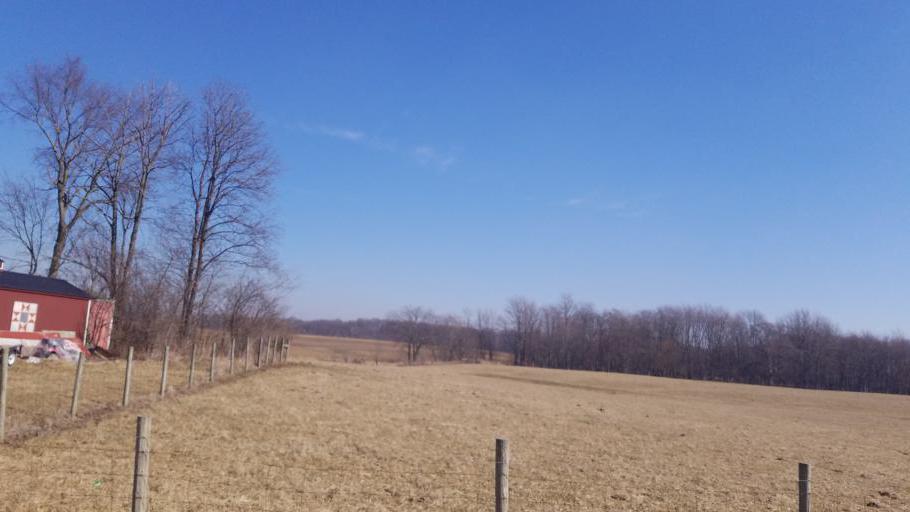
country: US
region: Ohio
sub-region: Richland County
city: Shelby
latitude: 40.8864
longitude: -82.5518
